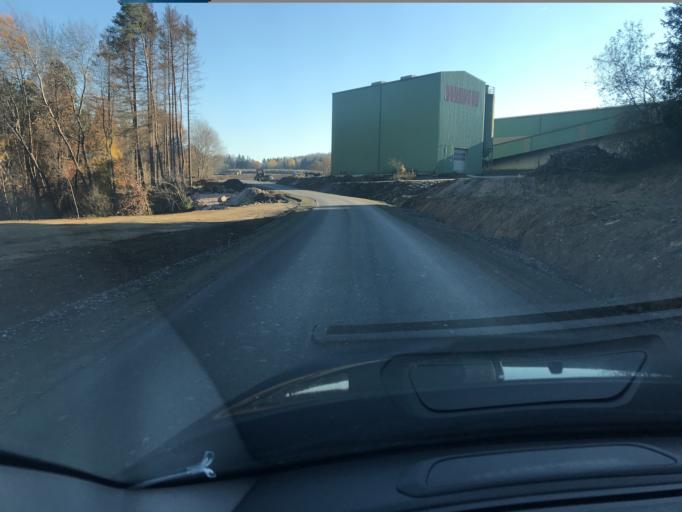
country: DE
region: Rheinland-Pfalz
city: Girod
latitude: 50.4457
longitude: 7.9240
